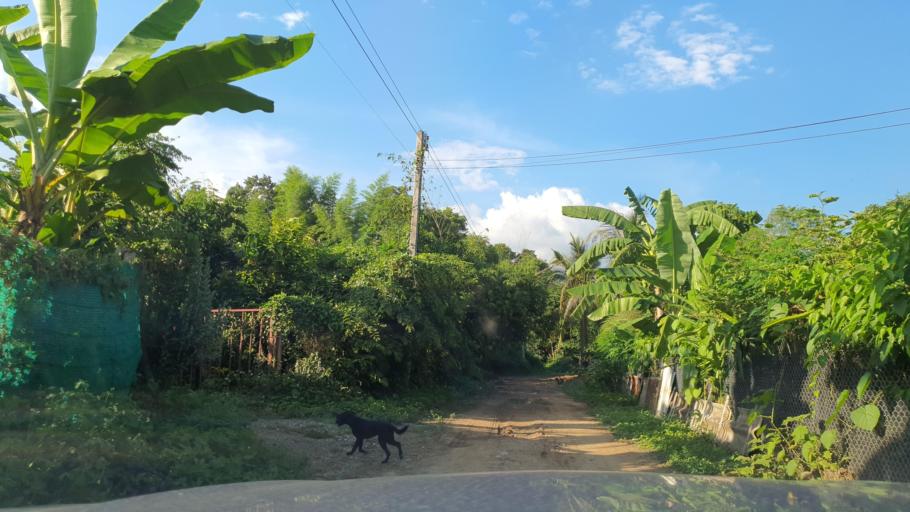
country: TH
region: Chiang Mai
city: Hang Dong
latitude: 18.7106
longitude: 98.8577
